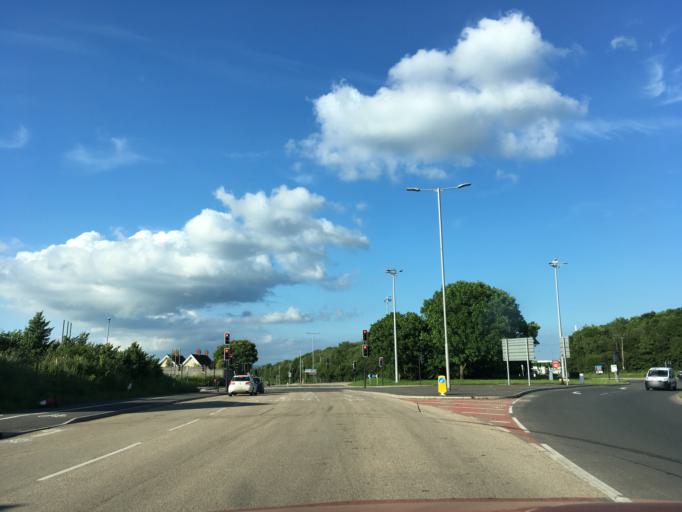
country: GB
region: England
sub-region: Somerset
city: North Petherton
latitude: 51.1034
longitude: -2.9989
